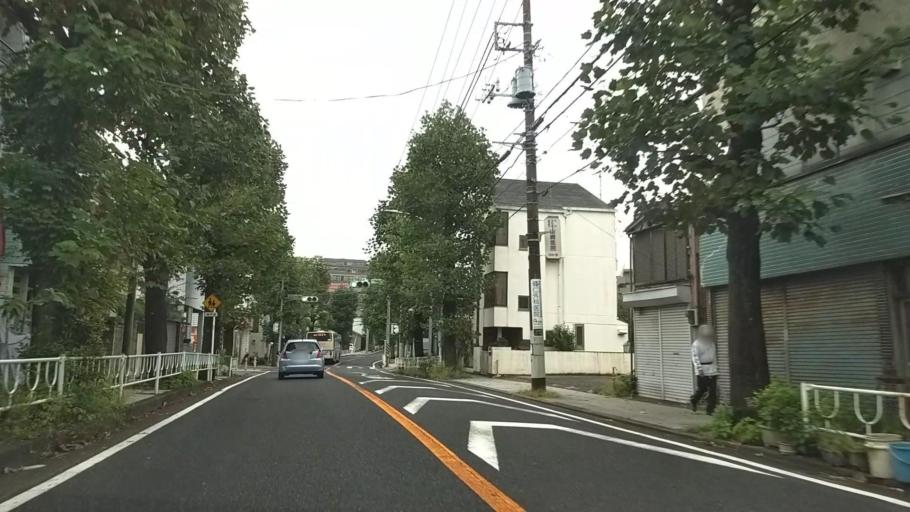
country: JP
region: Kanagawa
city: Yokohama
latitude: 35.4278
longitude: 139.6388
